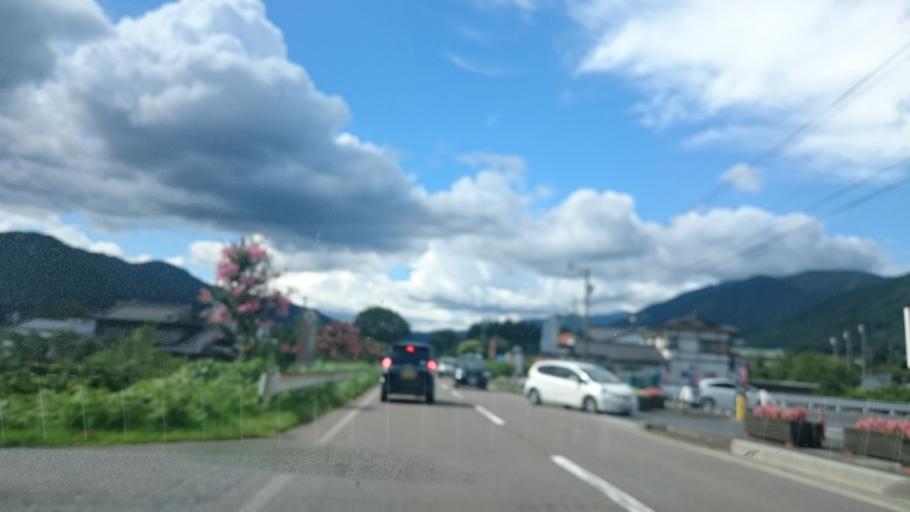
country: JP
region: Gifu
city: Nakatsugawa
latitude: 35.6399
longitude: 137.4444
